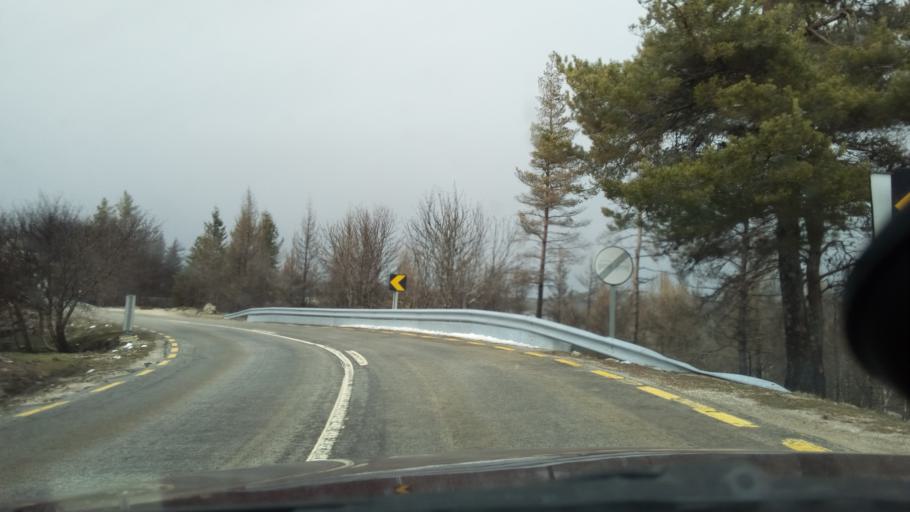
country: PT
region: Guarda
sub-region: Manteigas
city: Manteigas
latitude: 40.4128
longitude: -7.5808
